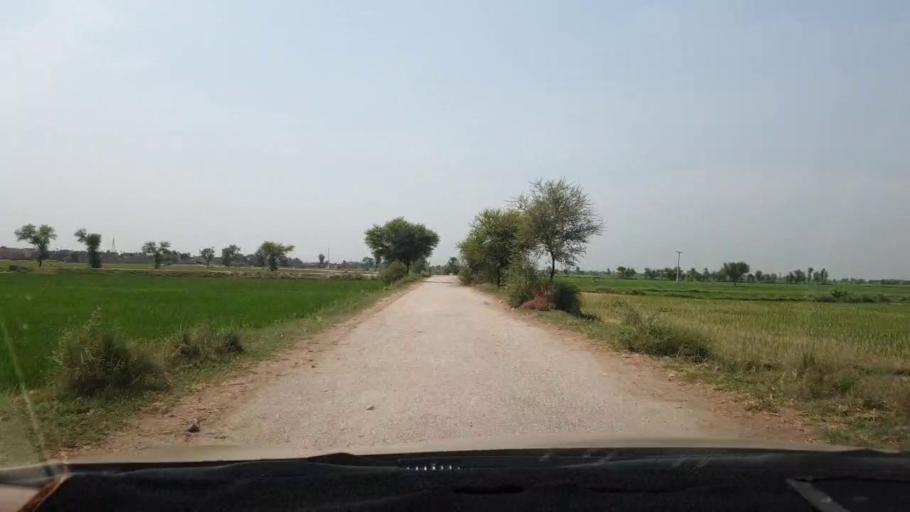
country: PK
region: Sindh
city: Naudero
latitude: 27.6377
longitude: 68.2735
